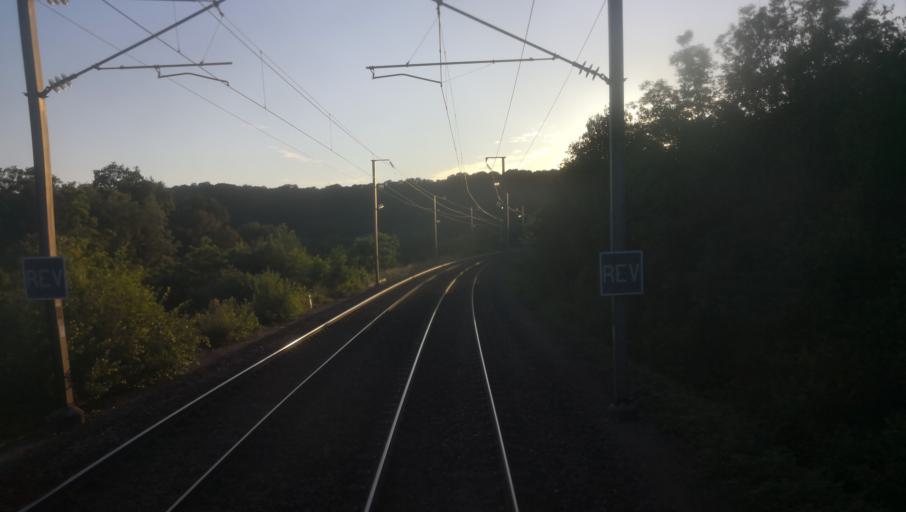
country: FR
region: Haute-Normandie
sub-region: Departement de l'Eure
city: Beaumont-le-Roger
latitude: 49.0334
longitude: 0.8113
